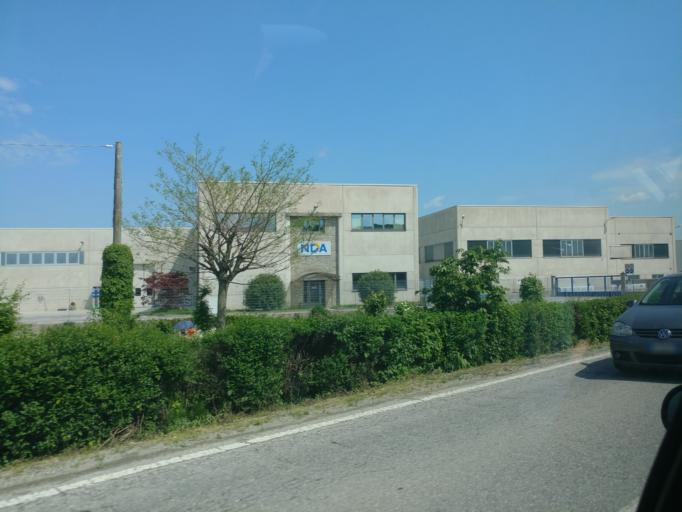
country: IT
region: Piedmont
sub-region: Provincia di Torino
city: Cavour
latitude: 44.7443
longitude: 7.4115
